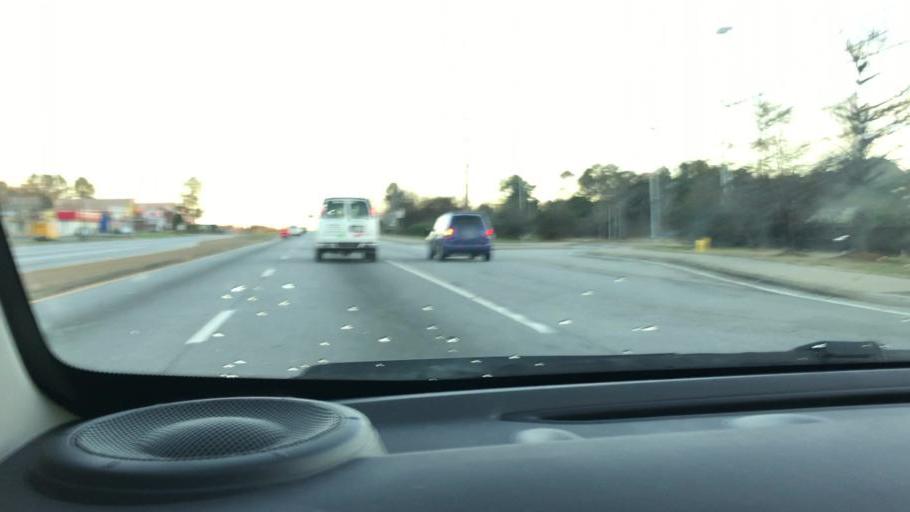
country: US
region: Georgia
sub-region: Clayton County
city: Riverdale
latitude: 33.5501
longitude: -84.4146
